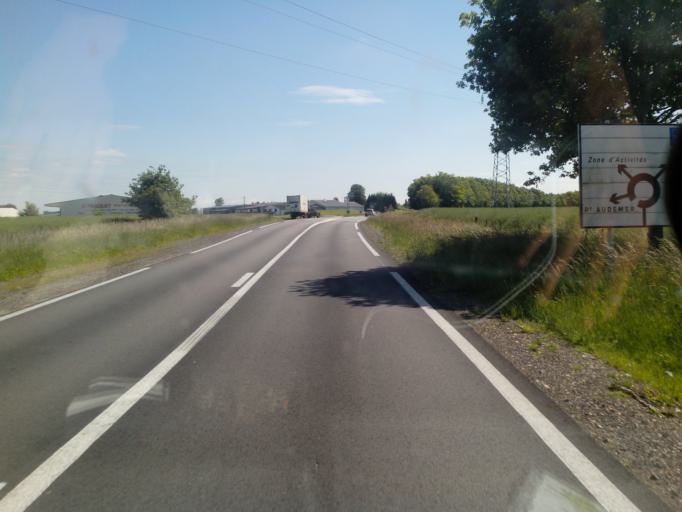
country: FR
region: Haute-Normandie
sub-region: Departement de l'Eure
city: Beuzeville
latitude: 49.3606
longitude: 0.3945
